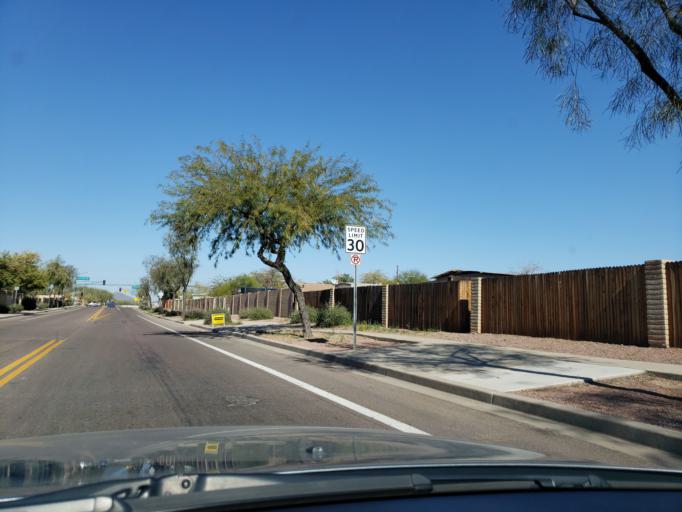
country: US
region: Arizona
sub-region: Maricopa County
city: Glendale
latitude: 33.6532
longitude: -112.0742
